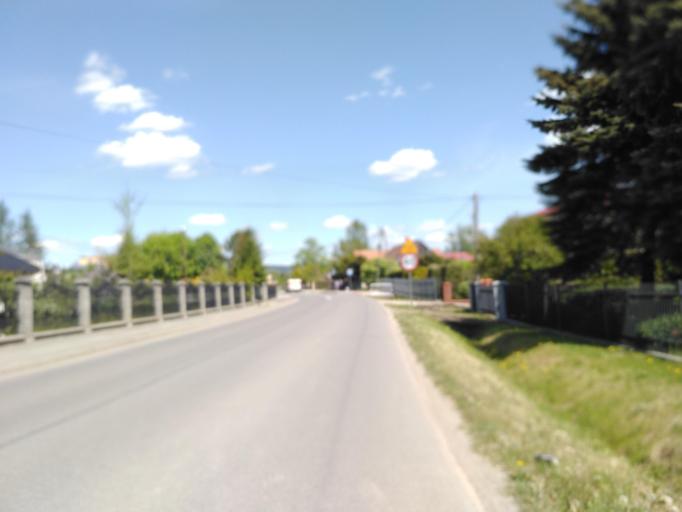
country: PL
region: Subcarpathian Voivodeship
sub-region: Powiat krosnienski
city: Odrzykon
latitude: 49.7180
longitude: 21.7110
